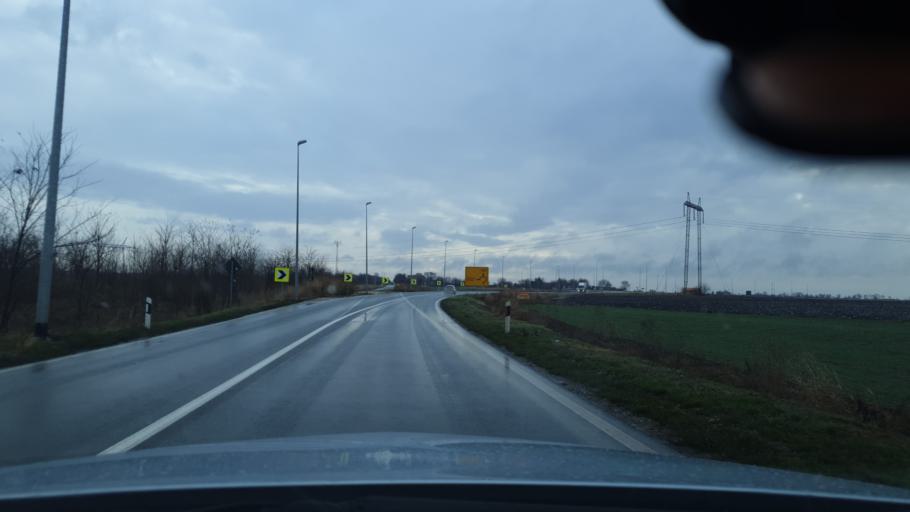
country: RS
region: Autonomna Pokrajina Vojvodina
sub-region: Juznobanatski Okrug
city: Kovin
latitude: 44.8261
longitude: 20.8481
